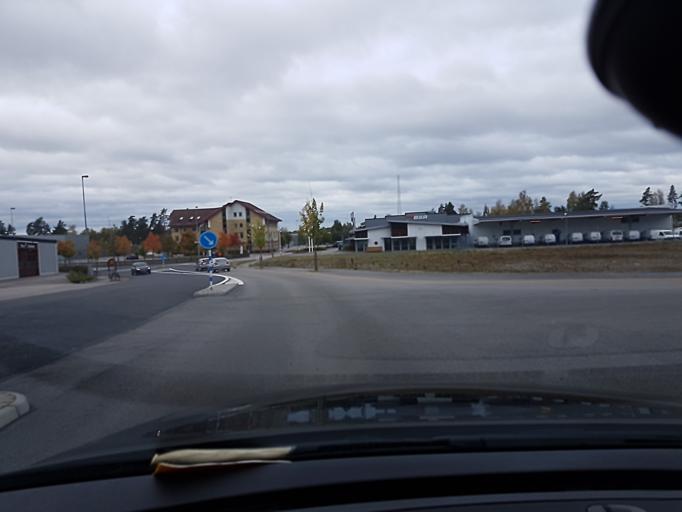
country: SE
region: Kronoberg
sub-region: Vaxjo Kommun
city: Vaexjoe
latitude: 56.9035
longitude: 14.8339
